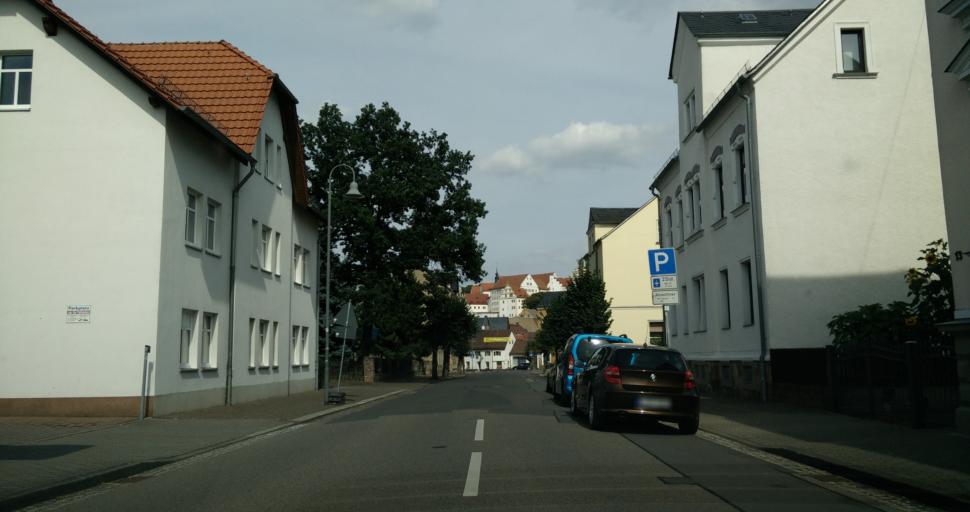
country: DE
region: Saxony
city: Colditz
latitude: 51.1270
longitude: 12.8037
